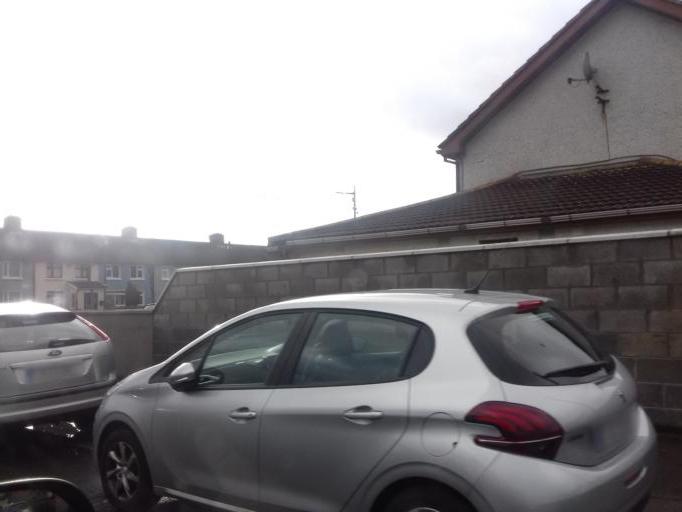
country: IE
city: Coolock
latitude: 53.3811
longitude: -6.1913
